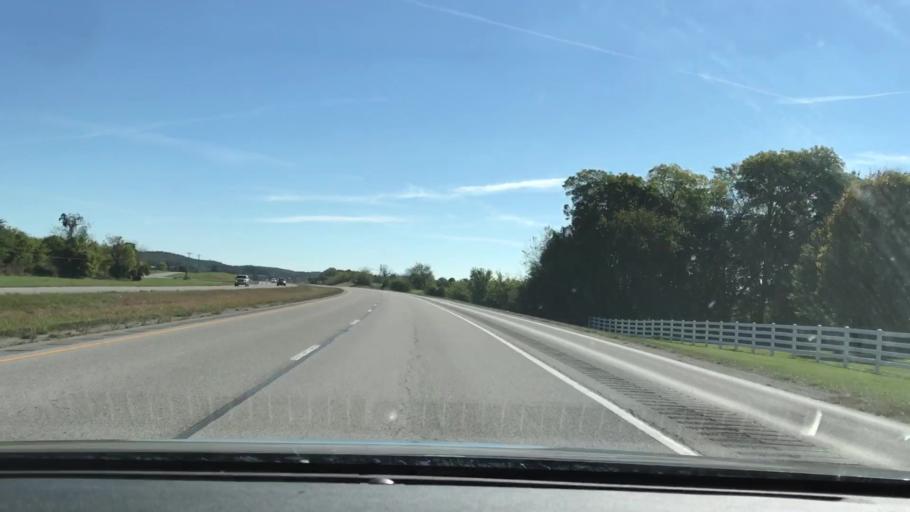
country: US
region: Kentucky
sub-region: Todd County
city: Elkton
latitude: 36.8422
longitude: -87.2646
